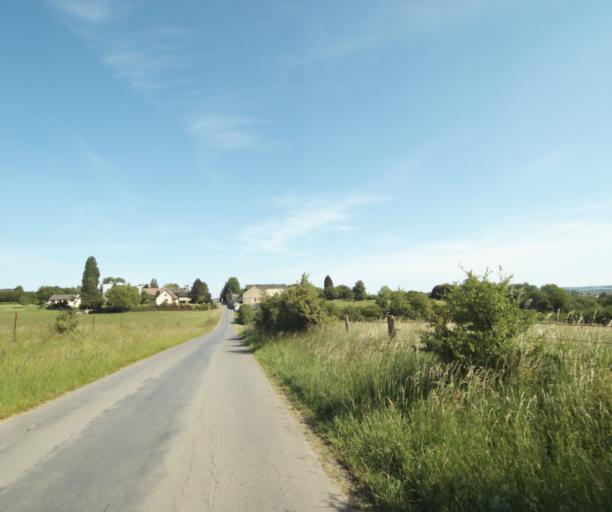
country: FR
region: Champagne-Ardenne
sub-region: Departement des Ardennes
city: Warcq
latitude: 49.7903
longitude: 4.6901
